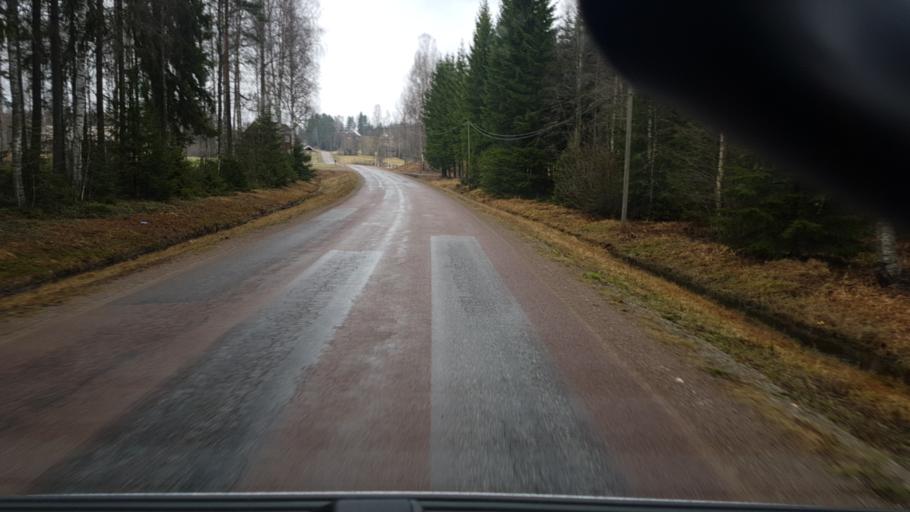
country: SE
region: Vaermland
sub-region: Eda Kommun
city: Amotfors
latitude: 59.9089
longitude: 12.5240
